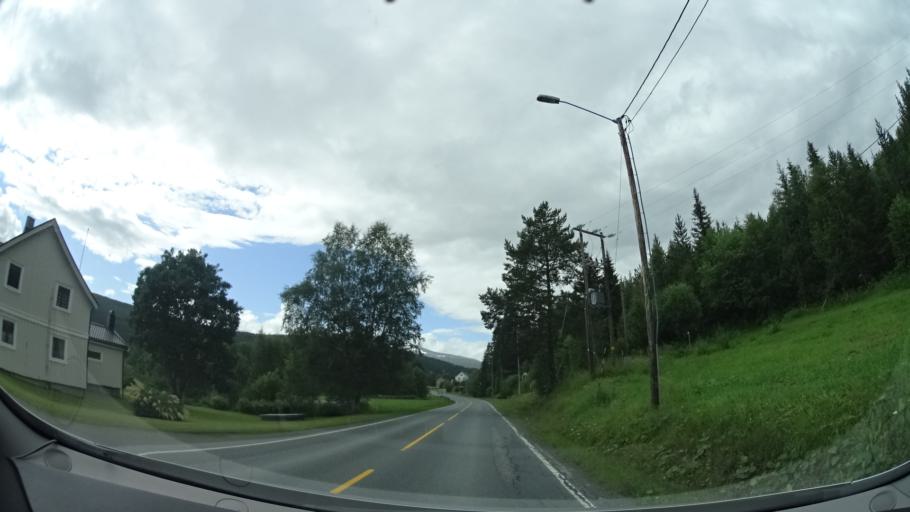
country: NO
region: Nord-Trondelag
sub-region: Meraker
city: Meraker
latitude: 63.3976
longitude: 11.7941
